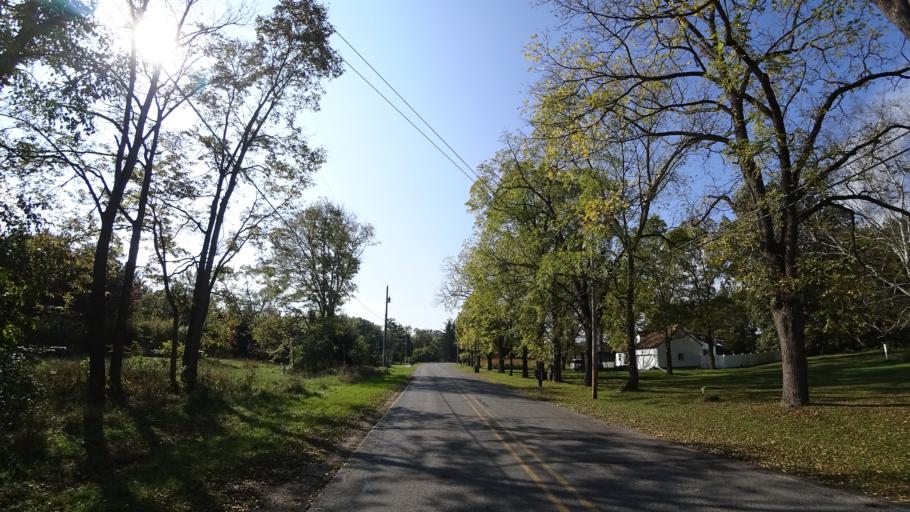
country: US
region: Michigan
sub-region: Saint Joseph County
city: Three Rivers
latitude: 41.9211
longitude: -85.6364
